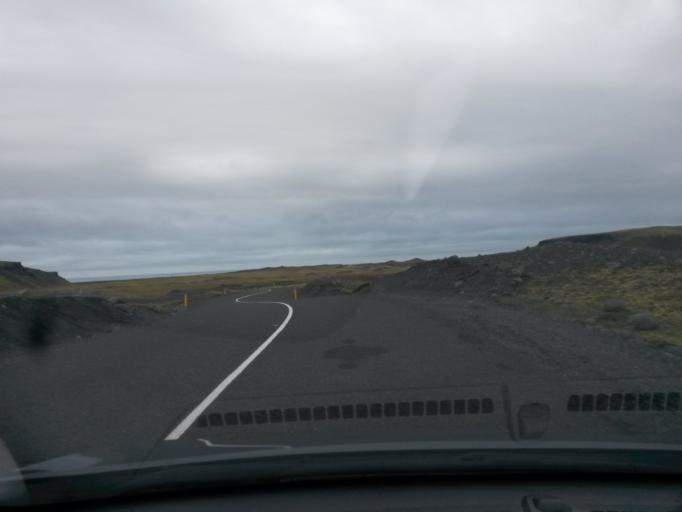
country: IS
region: South
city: Vestmannaeyjar
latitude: 63.5251
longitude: -19.3703
